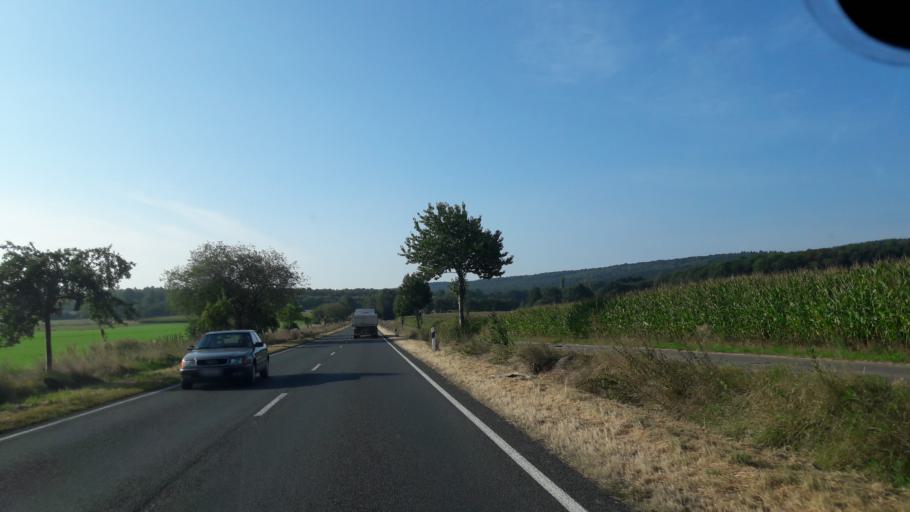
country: DE
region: Lower Saxony
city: Giesen
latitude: 52.1400
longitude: 9.8733
